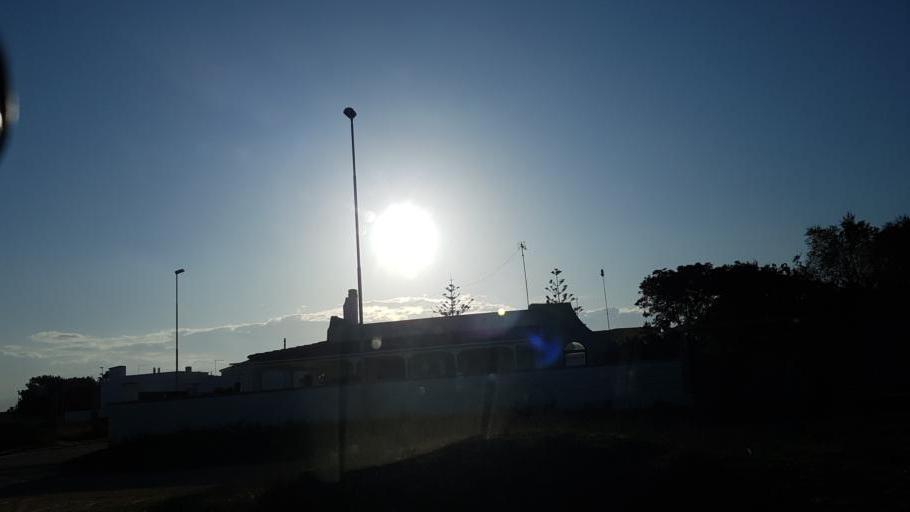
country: IT
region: Apulia
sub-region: Provincia di Brindisi
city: Torchiarolo
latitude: 40.5136
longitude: 18.1001
